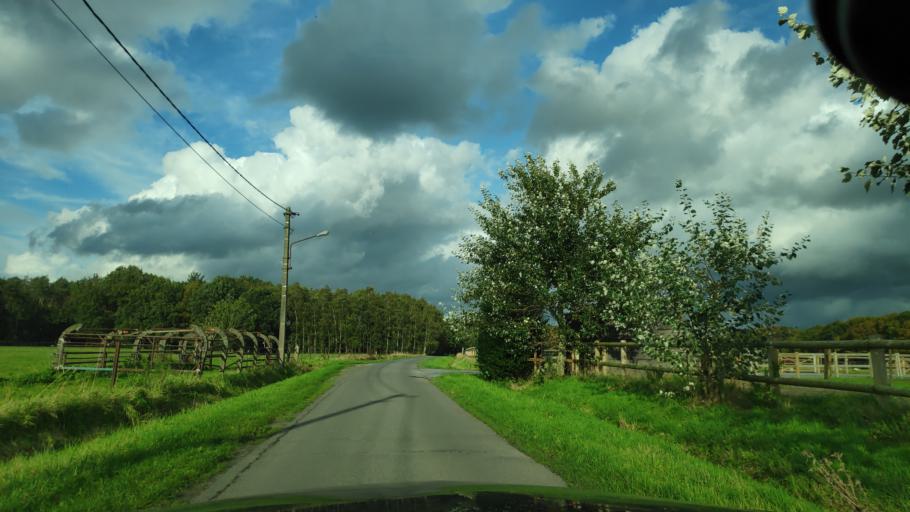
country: BE
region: Flanders
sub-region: Provincie Oost-Vlaanderen
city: Knesselare
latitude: 51.1469
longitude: 3.4452
